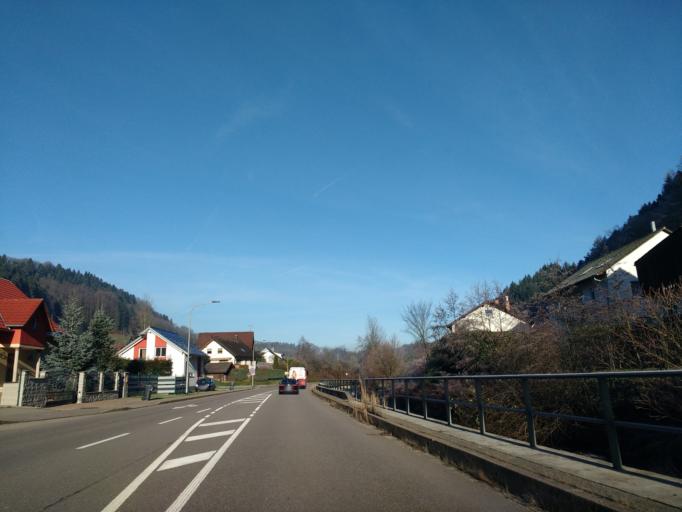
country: DE
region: Baden-Wuerttemberg
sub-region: Freiburg Region
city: Oppenau
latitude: 48.4561
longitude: 8.1629
